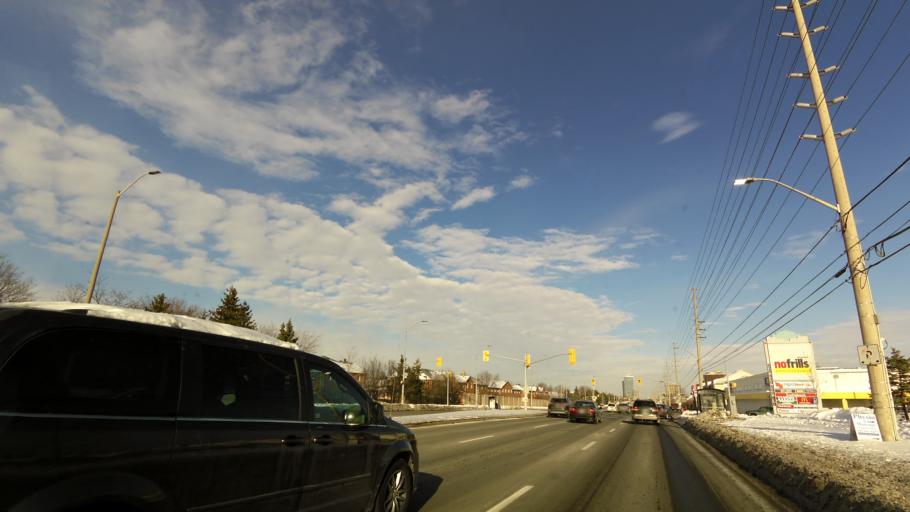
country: CA
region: Ontario
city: Mississauga
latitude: 43.5930
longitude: -79.6683
